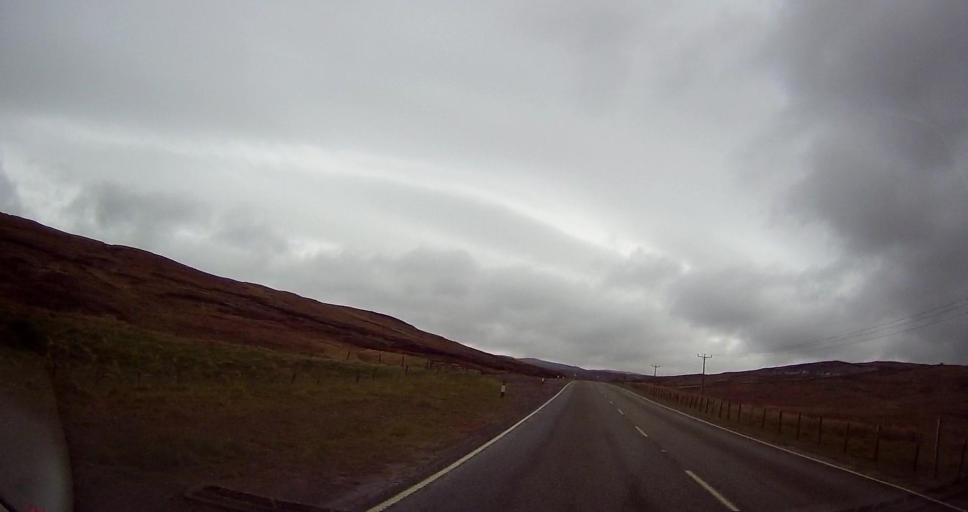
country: GB
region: Scotland
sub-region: Shetland Islands
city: Lerwick
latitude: 60.2690
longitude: -1.2330
